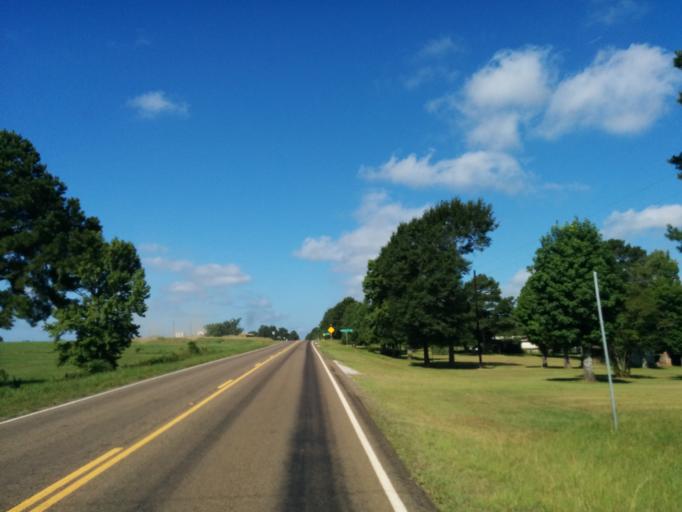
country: US
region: Texas
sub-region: Sabine County
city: Milam
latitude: 31.4218
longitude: -93.9709
